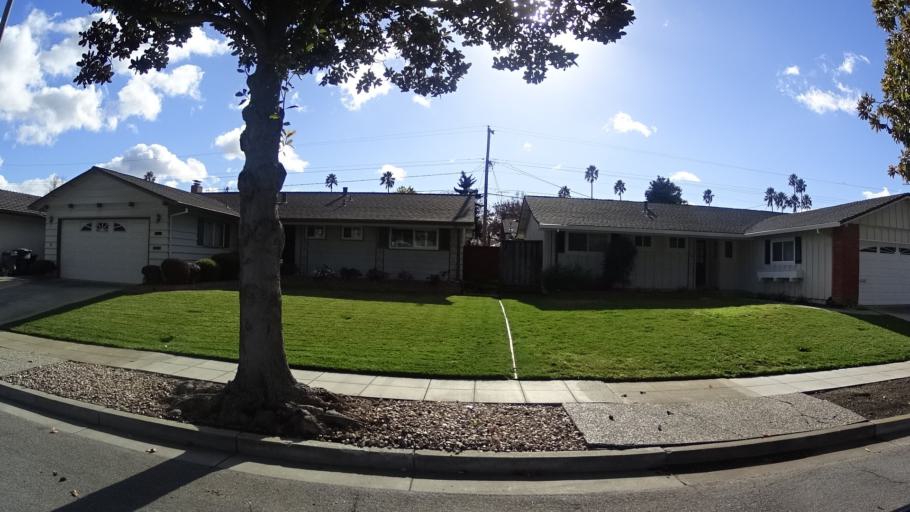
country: US
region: California
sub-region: Santa Clara County
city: Sunnyvale
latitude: 37.3760
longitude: -122.0526
